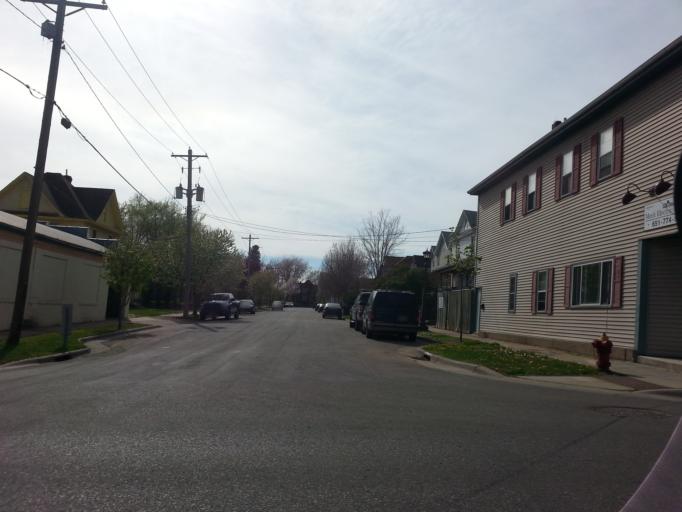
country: US
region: Minnesota
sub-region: Ramsey County
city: Saint Paul
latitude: 44.9639
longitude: -93.0736
